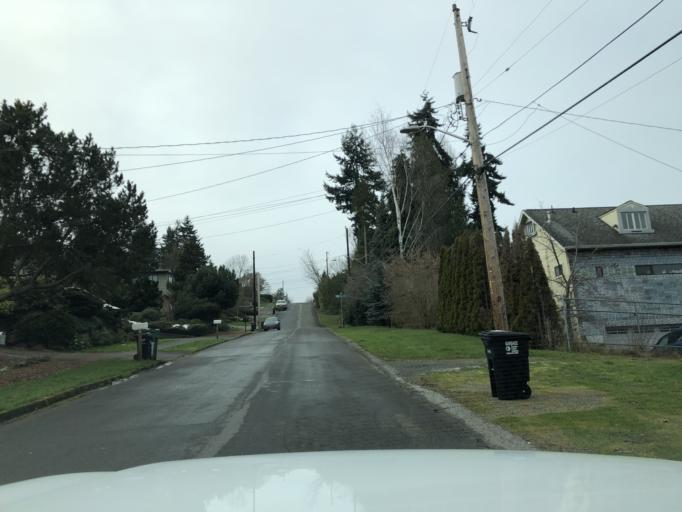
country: US
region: Washington
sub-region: King County
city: Lake Forest Park
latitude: 47.7011
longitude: -122.2884
